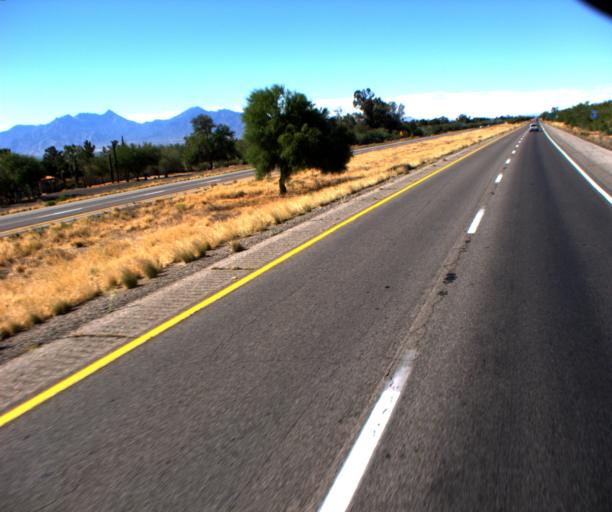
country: US
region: Arizona
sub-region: Pima County
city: Green Valley
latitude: 31.8988
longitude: -110.9859
